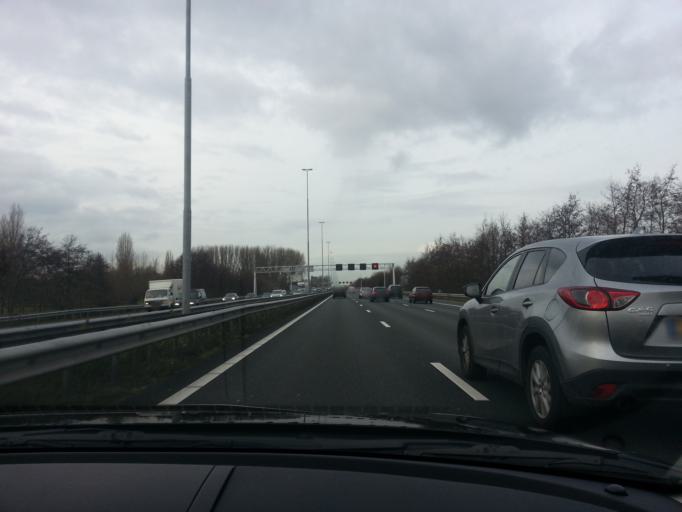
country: NL
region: South Holland
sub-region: Gemeente Schiedam
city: Schiedam
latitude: 51.9558
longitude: 4.4119
